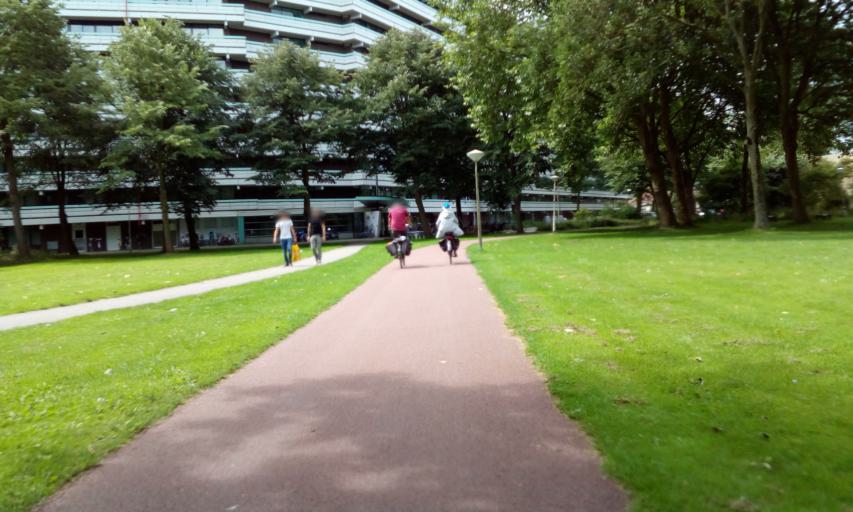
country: NL
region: South Holland
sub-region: Gemeente Zoetermeer
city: Zoetermeer
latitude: 52.0586
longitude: 4.4700
